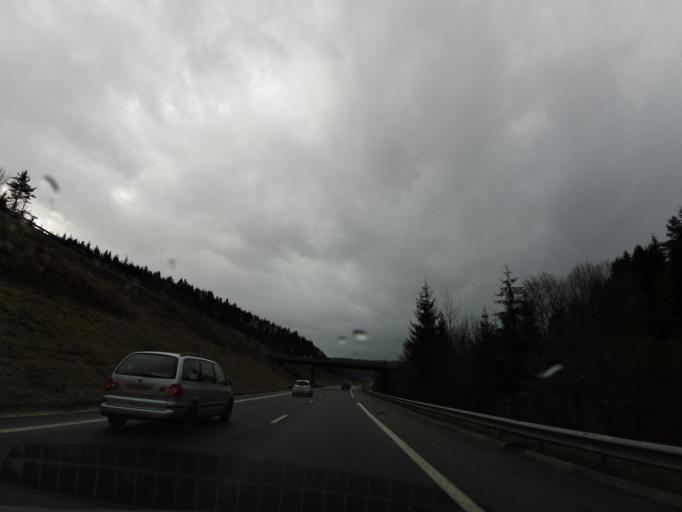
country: FR
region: Rhone-Alpes
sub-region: Departement de l'Ain
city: Saint-Martin-du-Frene
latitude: 46.1278
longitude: 5.5618
